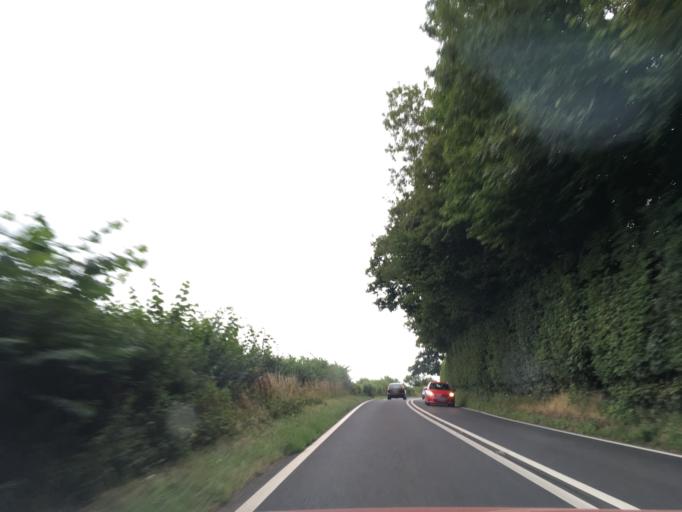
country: GB
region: Wales
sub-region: Sir Powys
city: Brecon
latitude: 51.9197
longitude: -3.3098
